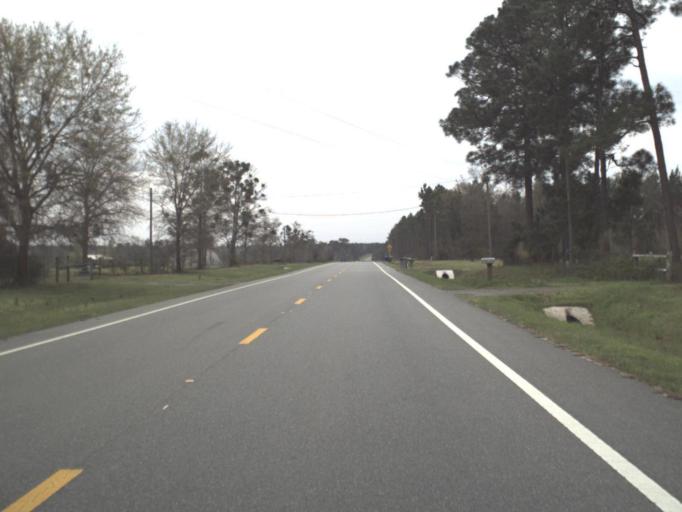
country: US
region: Florida
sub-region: Calhoun County
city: Blountstown
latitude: 30.3683
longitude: -85.2142
